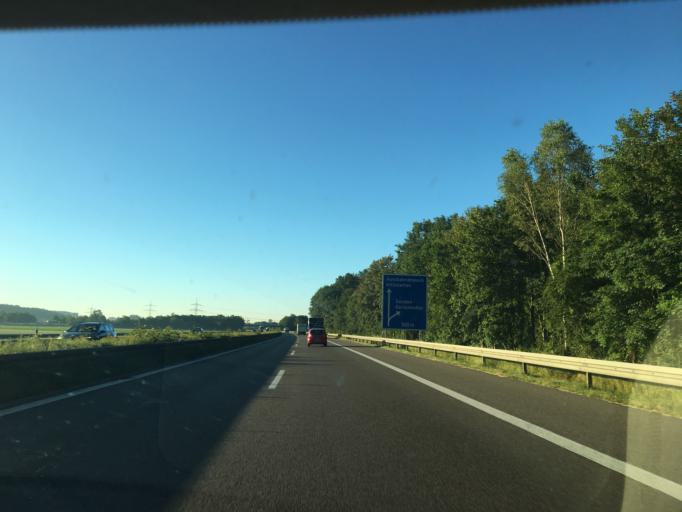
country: DE
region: Bavaria
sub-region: Swabia
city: Senden
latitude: 48.3429
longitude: 10.0239
